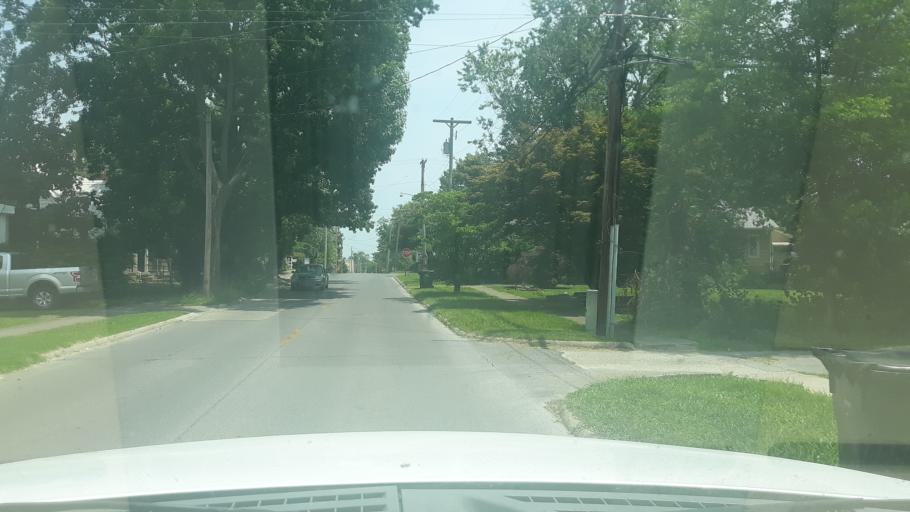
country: US
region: Illinois
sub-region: Saline County
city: Harrisburg
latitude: 37.7313
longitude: -88.5505
